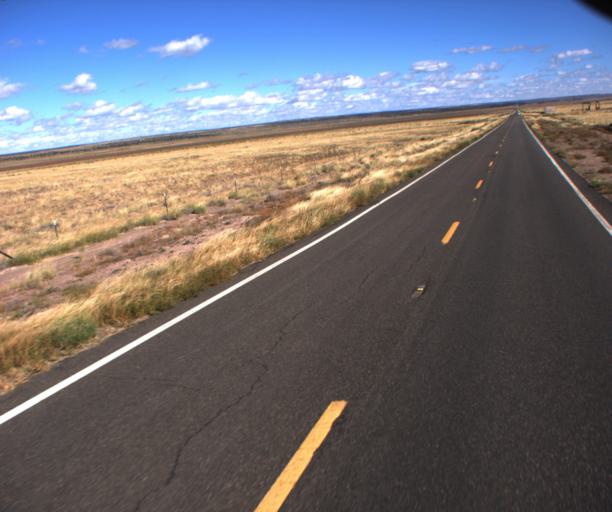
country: US
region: Arizona
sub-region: Apache County
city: Saint Johns
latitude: 34.6716
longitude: -109.2875
